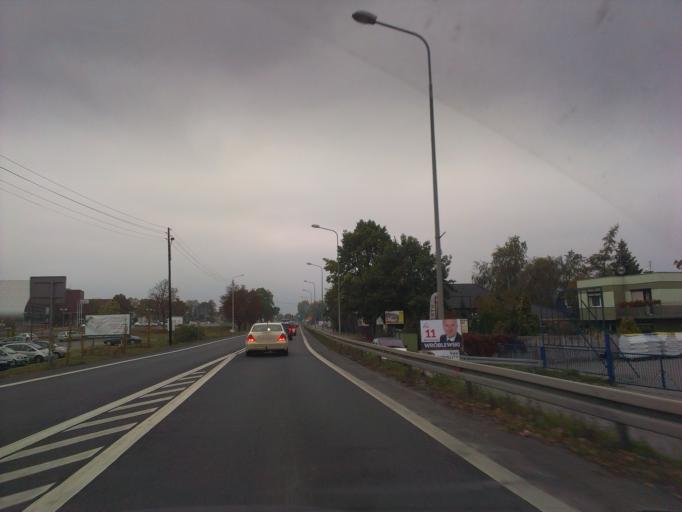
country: PL
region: Greater Poland Voivodeship
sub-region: Powiat poznanski
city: Suchy Las
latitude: 52.4736
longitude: 16.8763
